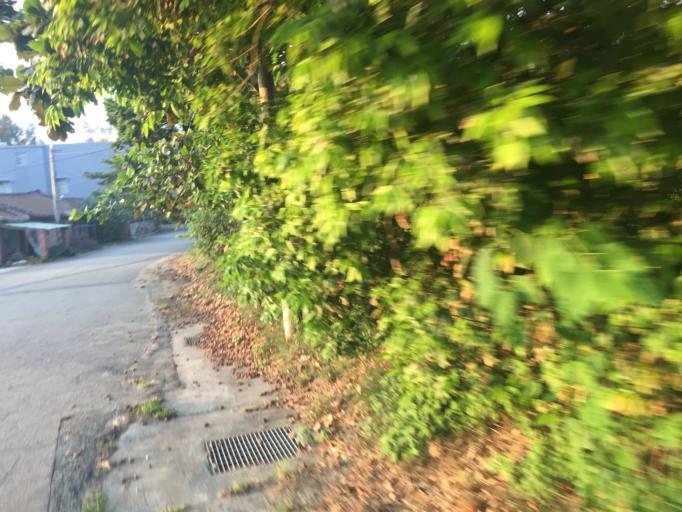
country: TW
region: Taiwan
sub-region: Hsinchu
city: Hsinchu
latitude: 24.7372
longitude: 120.8862
